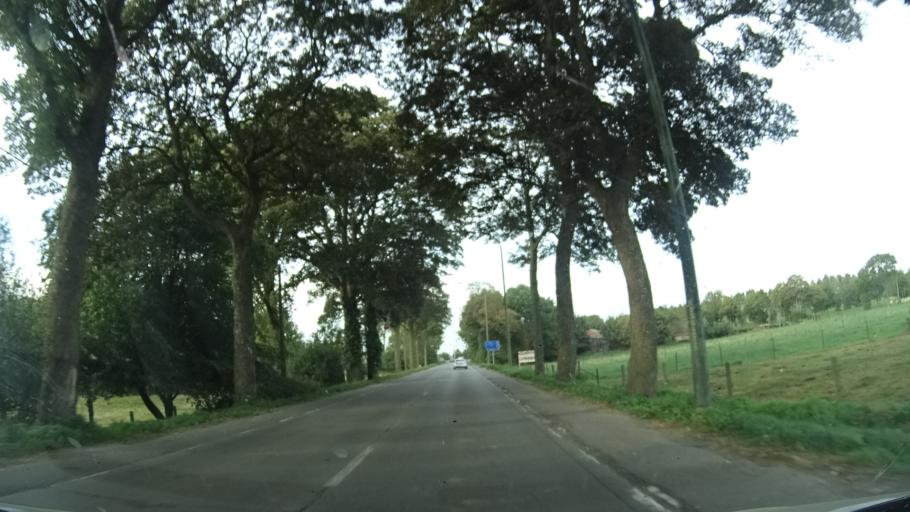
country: BE
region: Wallonia
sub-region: Province du Hainaut
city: Peruwelz
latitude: 50.5446
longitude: 3.6039
